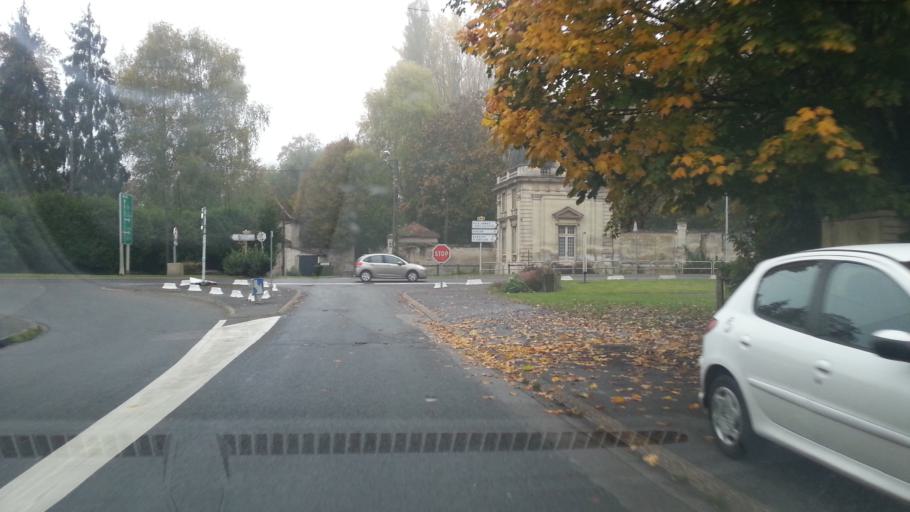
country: FR
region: Picardie
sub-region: Departement de l'Oise
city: Clermont
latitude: 49.3905
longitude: 2.4140
